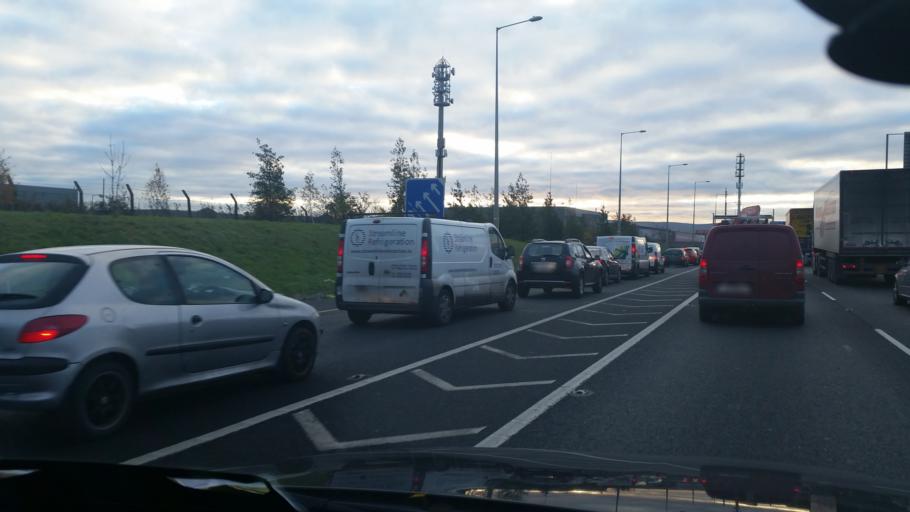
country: IE
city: Cherry Orchard
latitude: 53.3152
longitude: -6.3653
